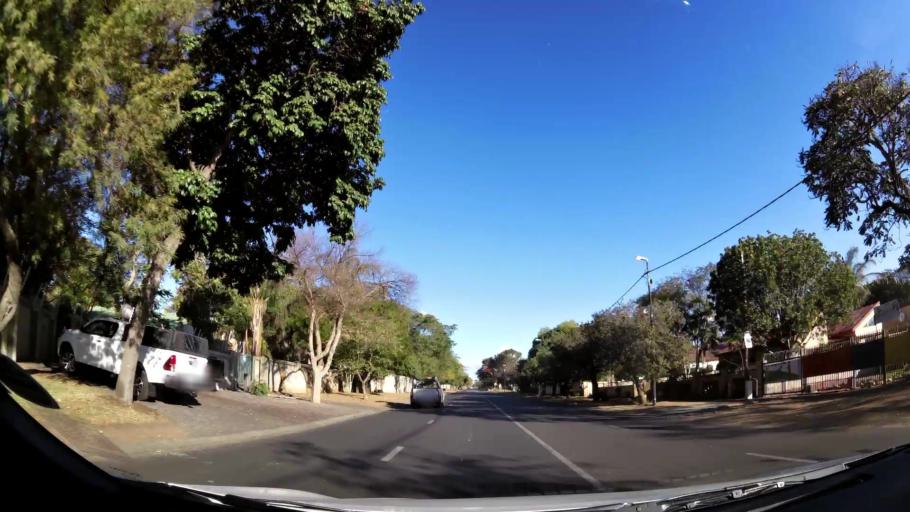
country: ZA
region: Limpopo
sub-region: Capricorn District Municipality
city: Polokwane
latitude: -23.8986
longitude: 29.4645
